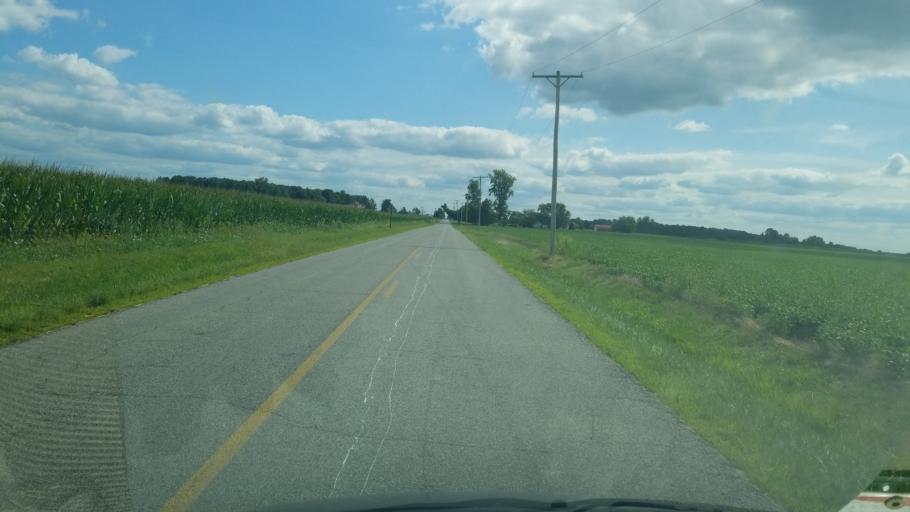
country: US
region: Ohio
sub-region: Logan County
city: Lakeview
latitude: 40.5566
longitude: -83.9748
